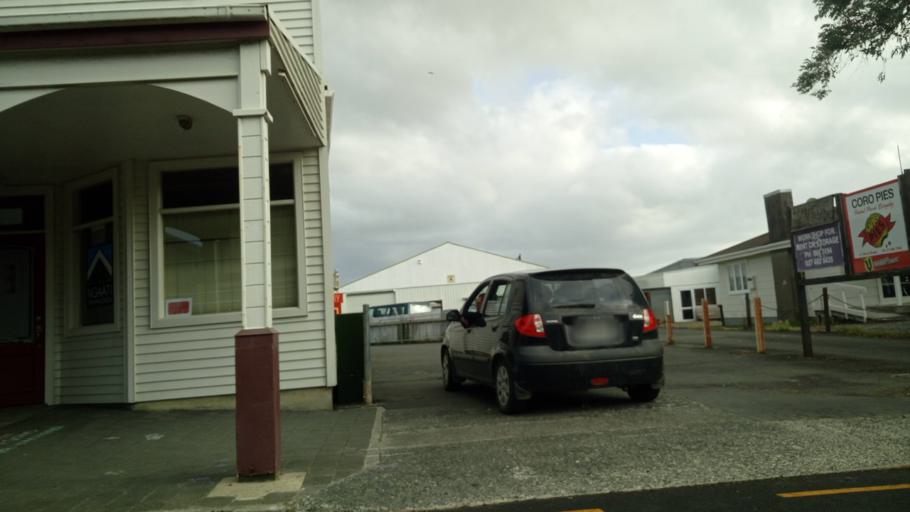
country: NZ
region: Waikato
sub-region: Thames-Coromandel District
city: Coromandel
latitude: -36.7603
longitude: 175.4968
